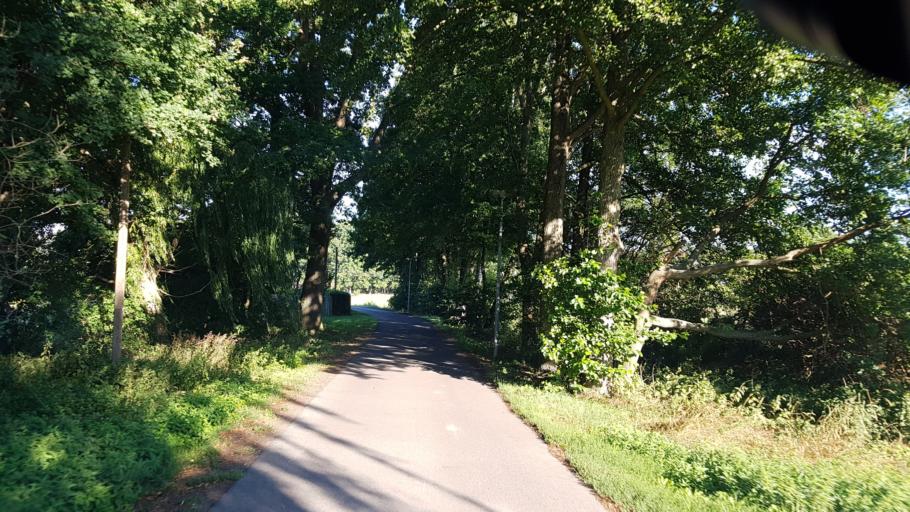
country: DE
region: Brandenburg
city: Calau
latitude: 51.7459
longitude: 13.9169
